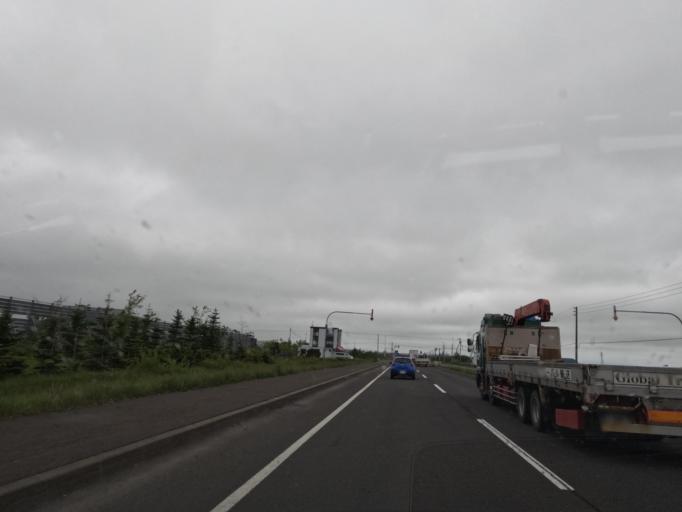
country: JP
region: Hokkaido
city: Tobetsu
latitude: 43.1770
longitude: 141.5222
